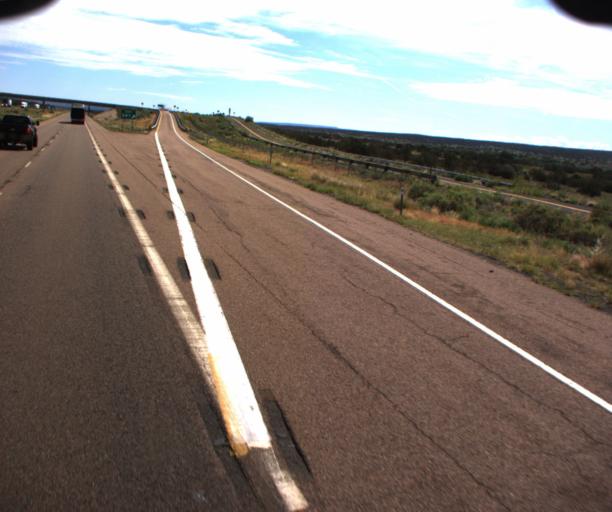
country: US
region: Arizona
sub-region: Apache County
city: Houck
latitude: 35.2359
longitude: -109.3053
